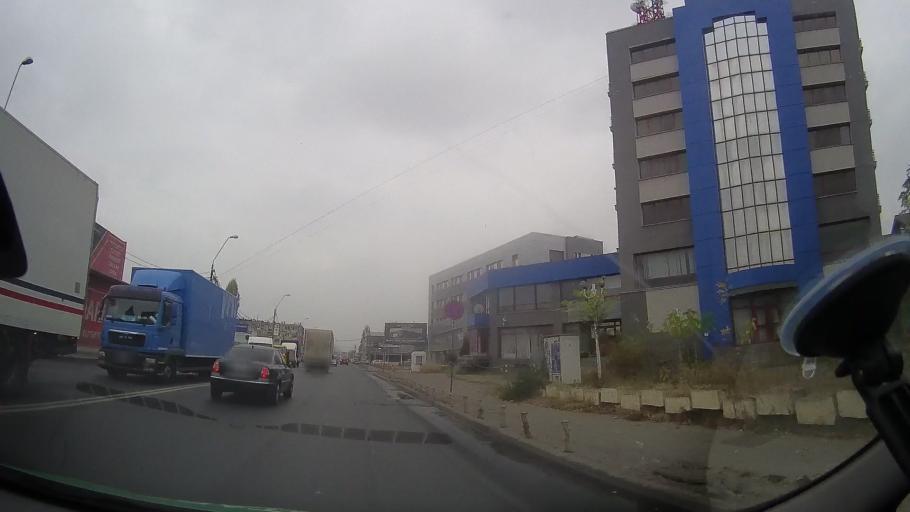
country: RO
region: Ilfov
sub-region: Comuna Chiajna
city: Rosu
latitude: 44.4306
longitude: 26.0037
